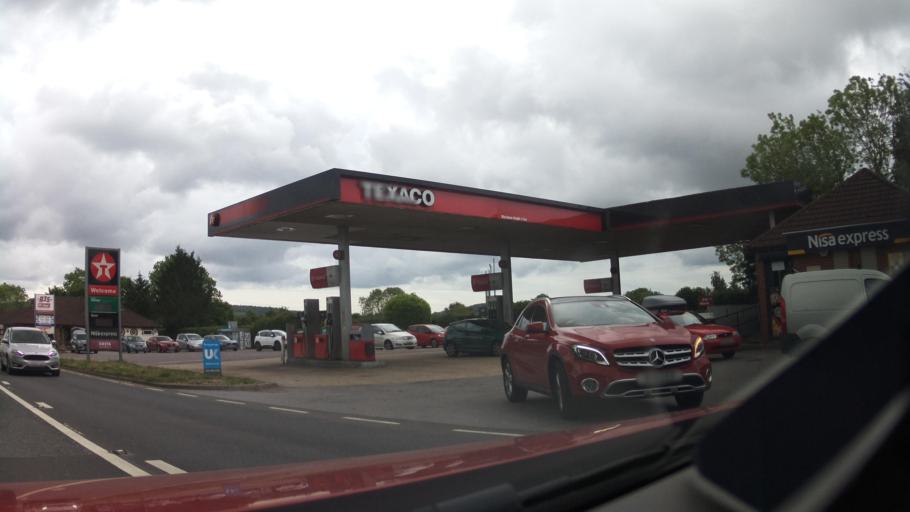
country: GB
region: England
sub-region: Devon
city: Axminster
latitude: 50.7789
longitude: -3.0315
